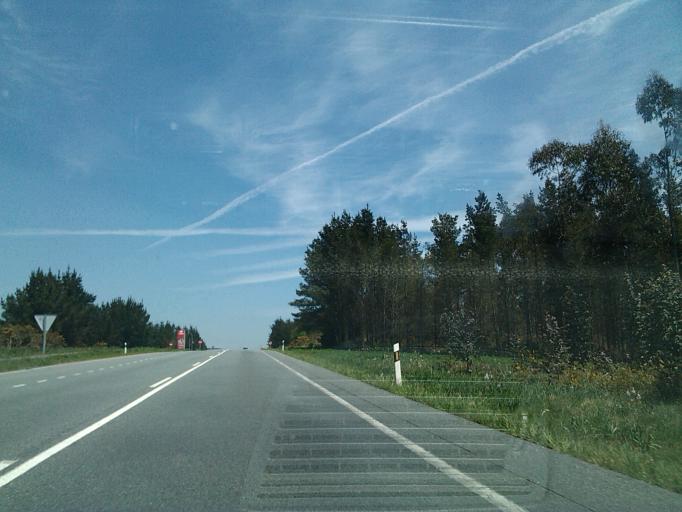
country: ES
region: Galicia
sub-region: Provincia da Coruna
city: Aranga
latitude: 43.1794
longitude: -7.9696
